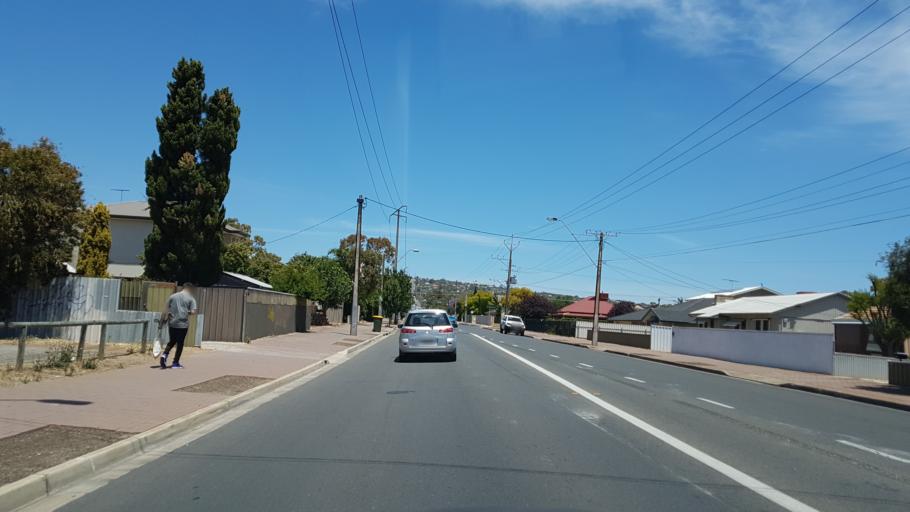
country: AU
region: South Australia
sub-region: Marion
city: Sturt
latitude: -35.0193
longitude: 138.5411
